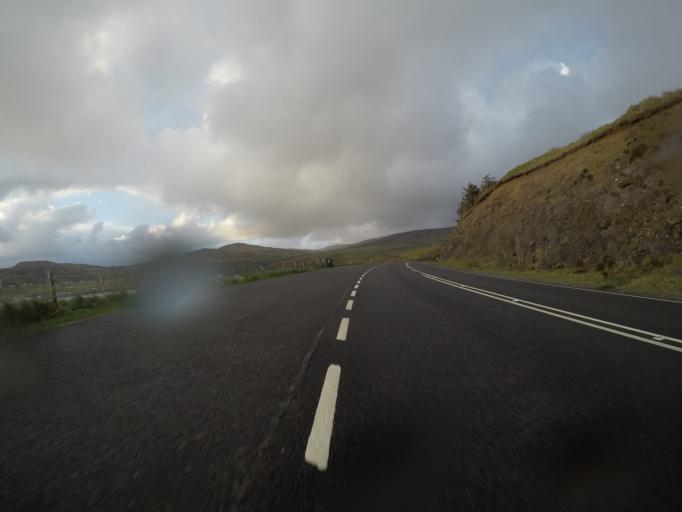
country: GB
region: Scotland
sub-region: Highland
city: Portree
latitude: 57.5777
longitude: -6.3651
